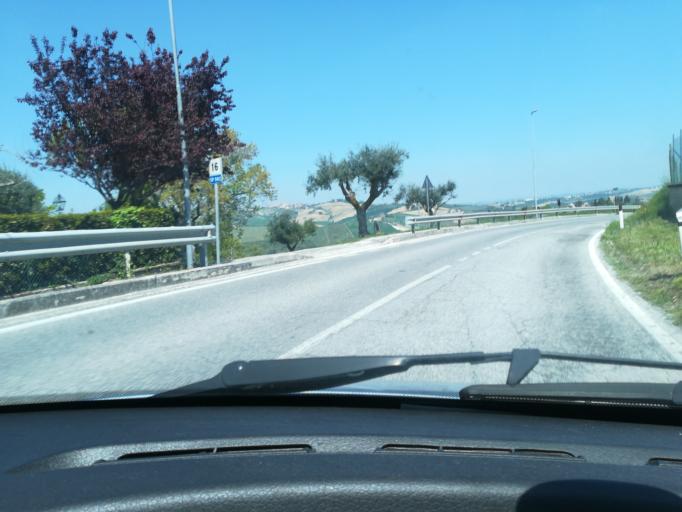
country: IT
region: The Marches
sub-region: Provincia di Macerata
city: Strada
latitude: 43.3955
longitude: 13.2054
